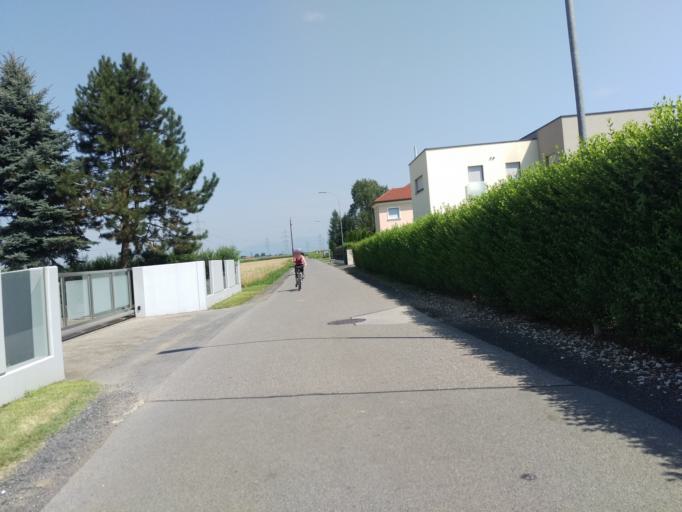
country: AT
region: Styria
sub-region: Politischer Bezirk Graz-Umgebung
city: Werndorf
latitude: 46.9263
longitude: 15.4901
